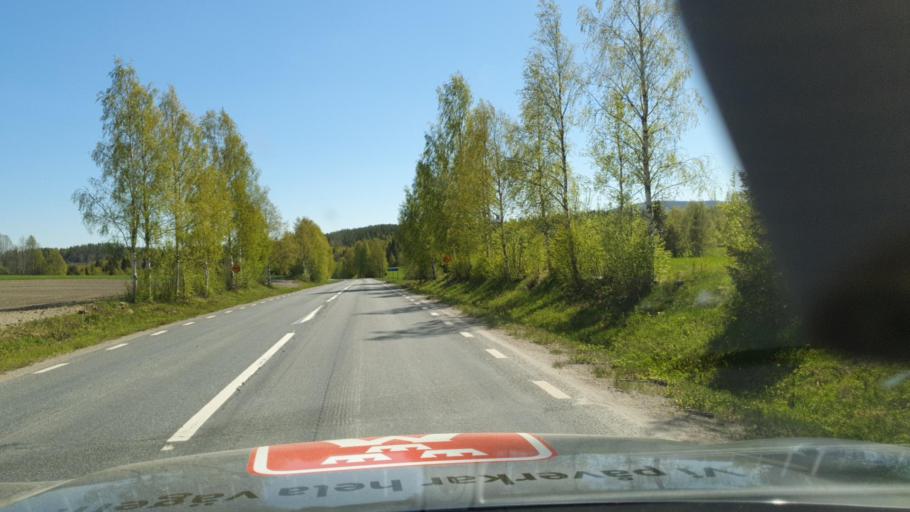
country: SE
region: Vaesternorrland
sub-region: OErnskoeldsviks Kommun
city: Ornskoldsvik
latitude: 63.6509
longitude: 18.5410
